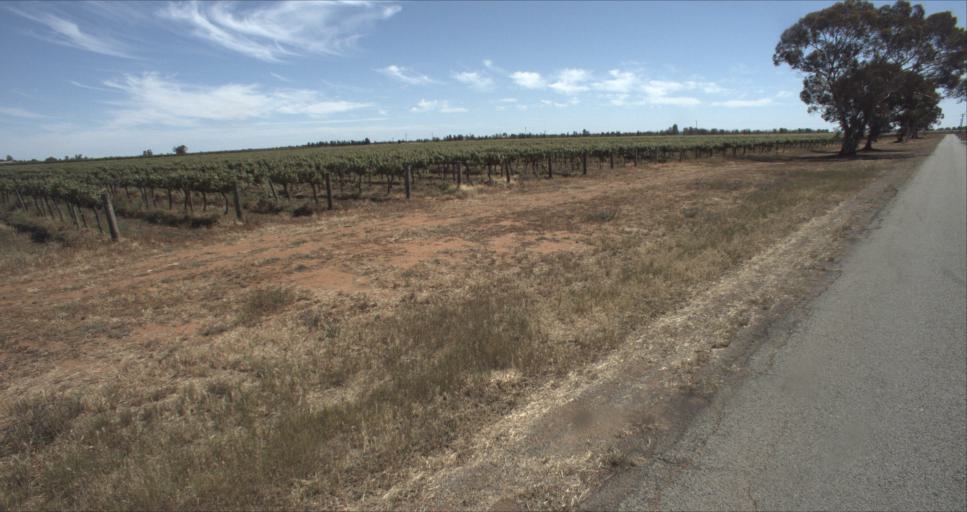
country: AU
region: New South Wales
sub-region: Leeton
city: Leeton
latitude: -34.5550
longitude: 146.3819
